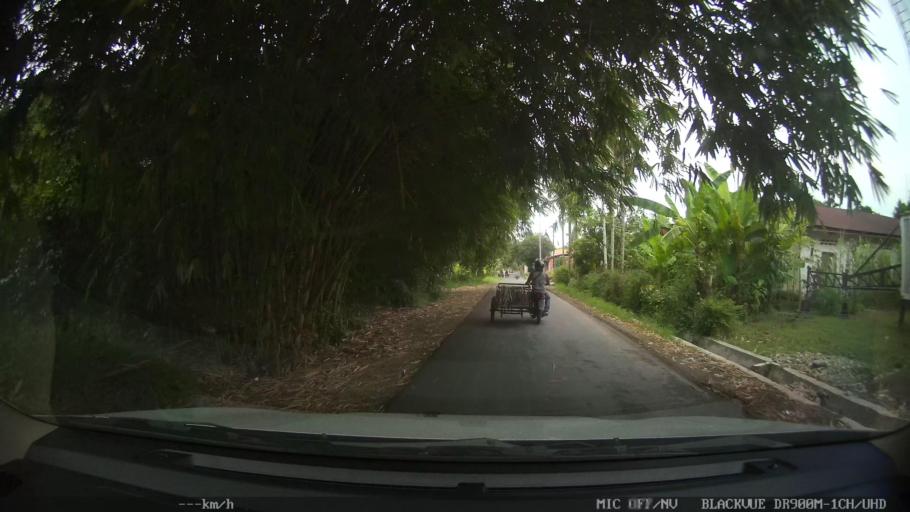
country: ID
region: North Sumatra
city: Sunggal
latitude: 3.6211
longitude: 98.5914
